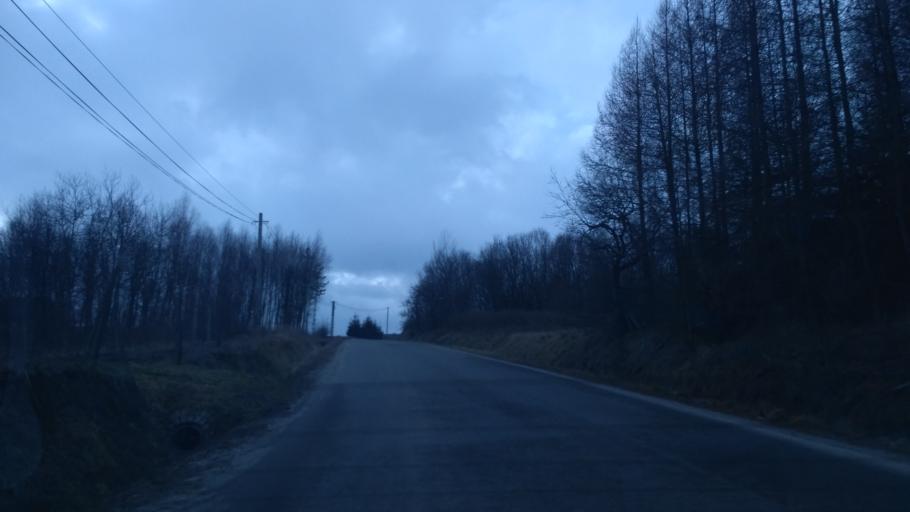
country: PL
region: Subcarpathian Voivodeship
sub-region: Powiat rzeszowski
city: Blazowa
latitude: 49.8720
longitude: 22.1001
